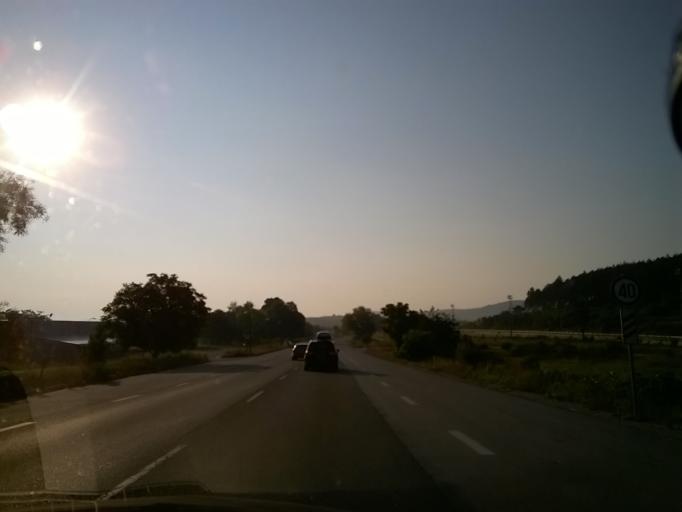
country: BG
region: Sofiya
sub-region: Obshtina Dragoman
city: Dragoman
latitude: 42.9314
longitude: 22.9256
